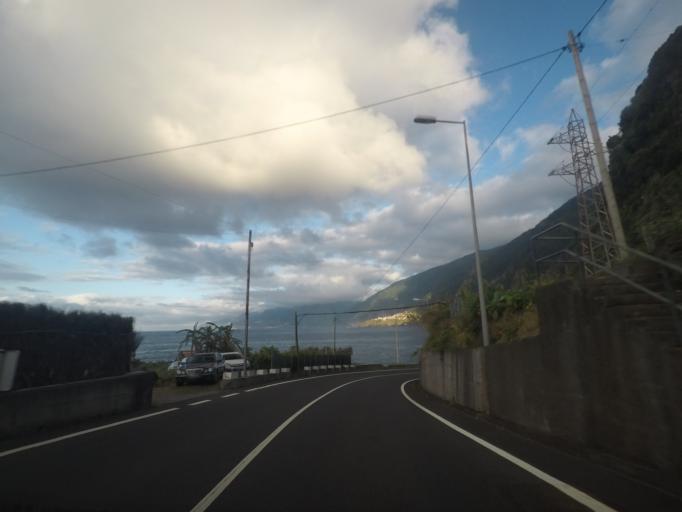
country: PT
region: Madeira
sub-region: Porto Moniz
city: Porto Moniz
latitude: 32.8419
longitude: -17.1417
